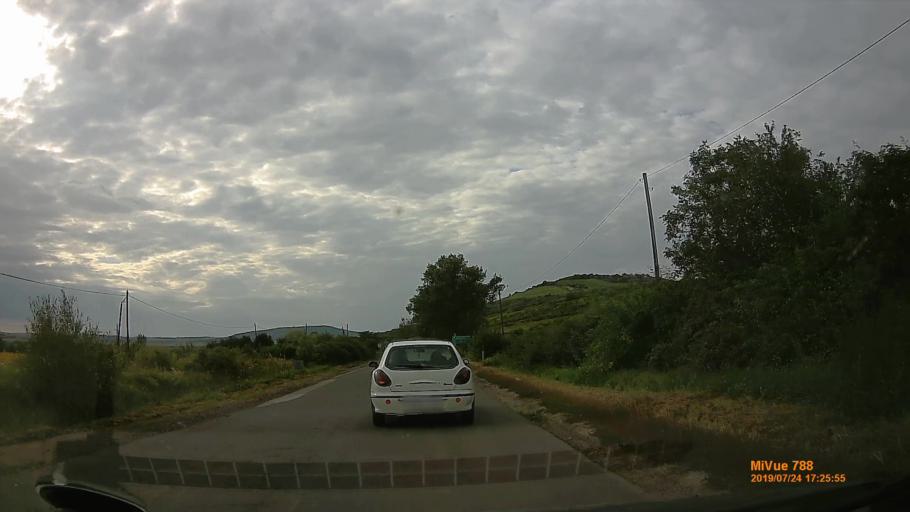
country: HU
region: Borsod-Abauj-Zemplen
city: Tallya
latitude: 48.2413
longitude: 21.2066
